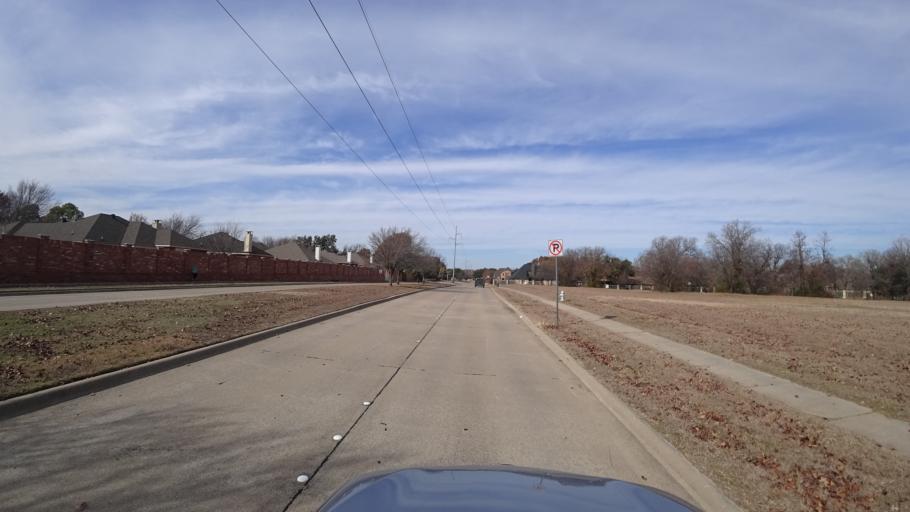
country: US
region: Texas
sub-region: Denton County
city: Highland Village
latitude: 33.0787
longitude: -97.0381
